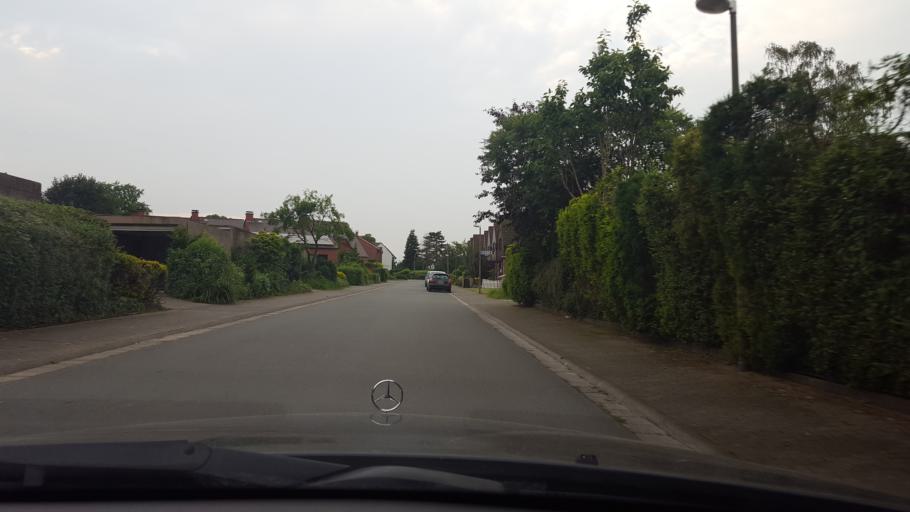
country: DE
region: North Rhine-Westphalia
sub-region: Regierungsbezirk Munster
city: Recklinghausen
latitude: 51.6672
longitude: 7.1857
